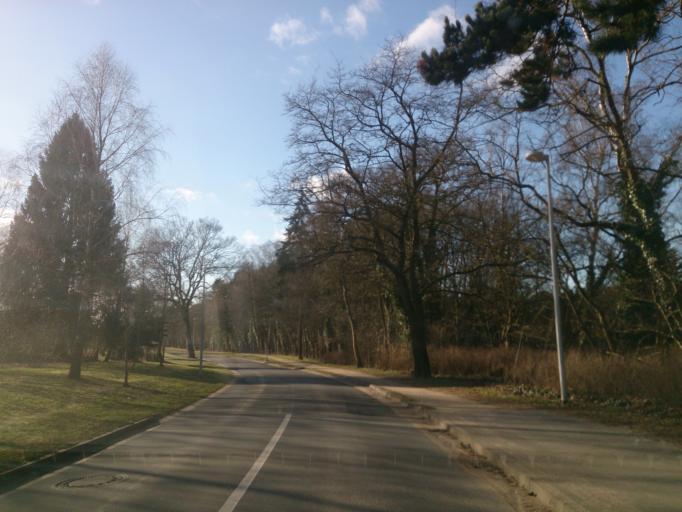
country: DE
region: Mecklenburg-Vorpommern
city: Malchow
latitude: 53.4749
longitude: 12.4180
